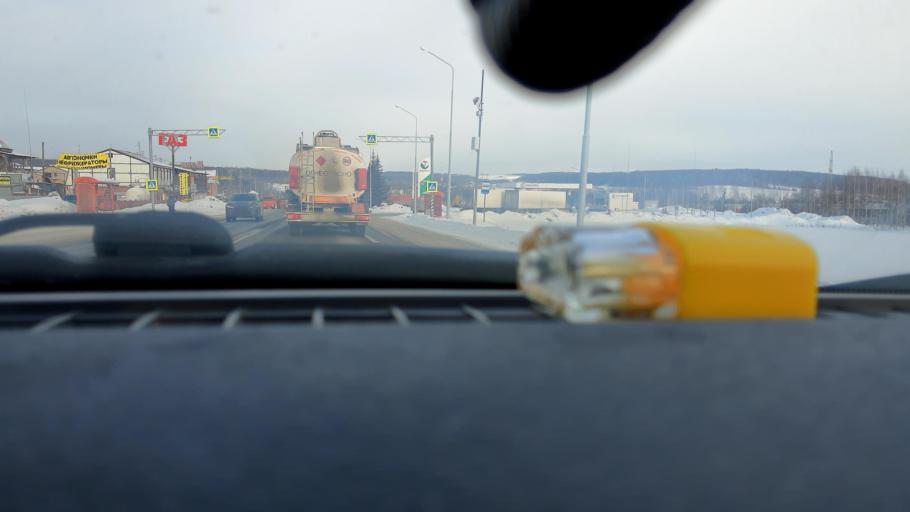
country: RU
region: Bashkortostan
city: Iglino
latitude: 54.7599
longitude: 56.3884
